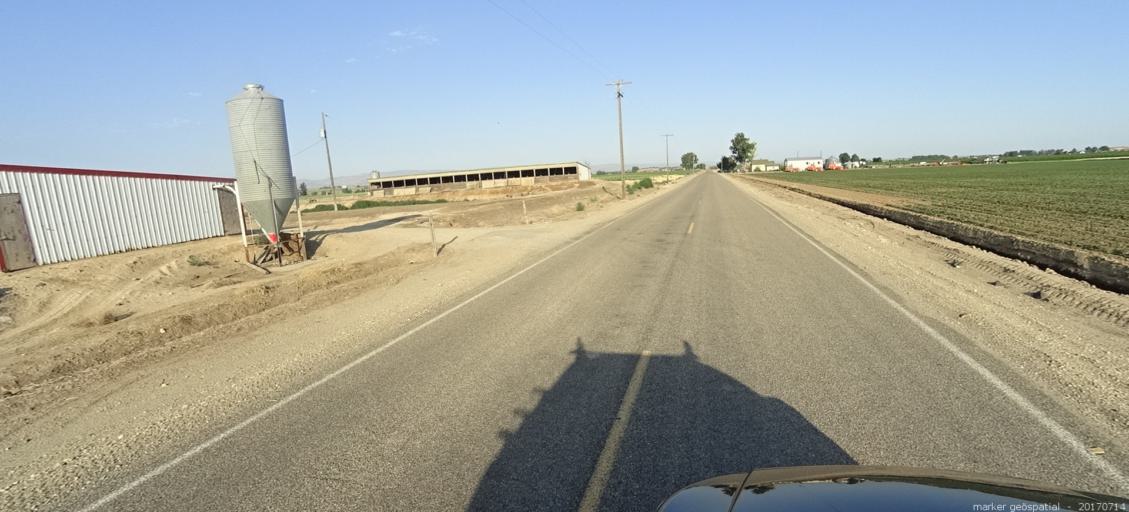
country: US
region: Idaho
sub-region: Ada County
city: Kuna
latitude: 43.4593
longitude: -116.4996
